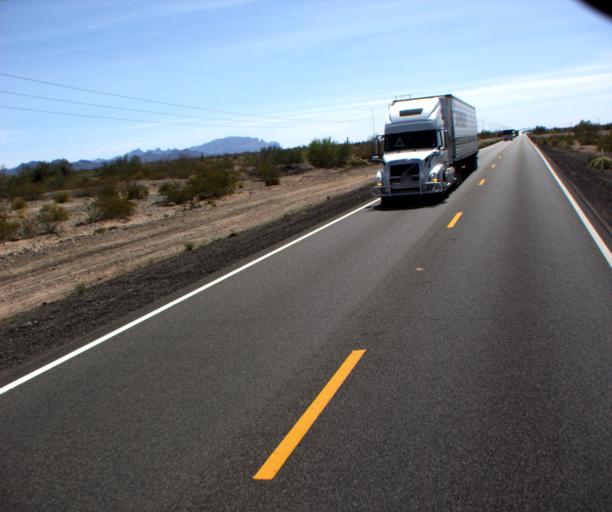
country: US
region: Arizona
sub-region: La Paz County
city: Quartzsite
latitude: 33.5887
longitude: -114.2171
